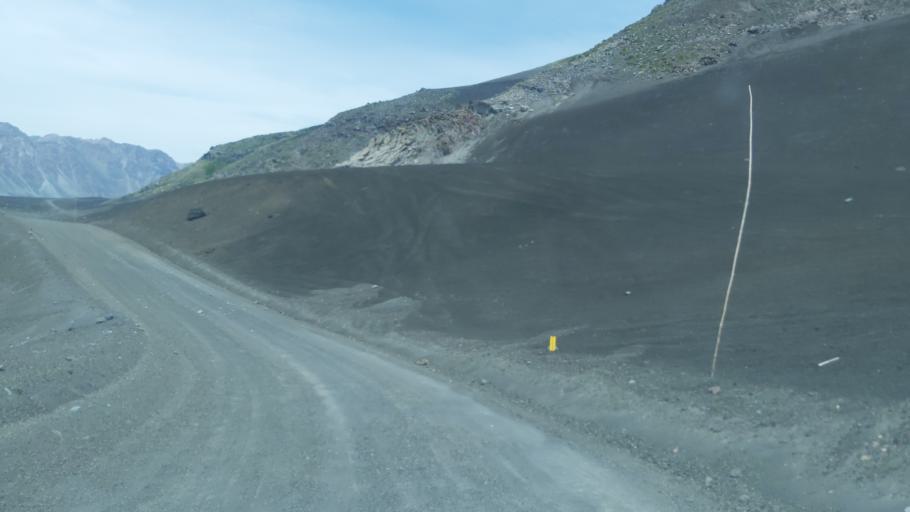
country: AR
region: Neuquen
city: Andacollo
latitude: -37.4038
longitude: -71.3022
